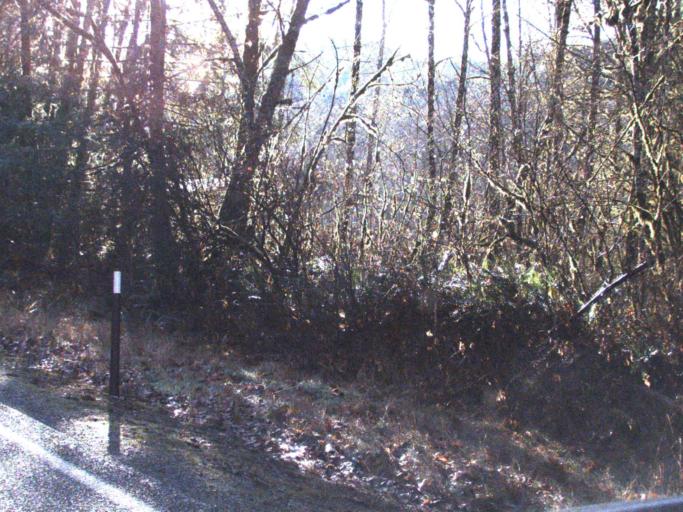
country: US
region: Washington
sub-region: Snohomish County
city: Darrington
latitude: 48.4377
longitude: -121.5764
